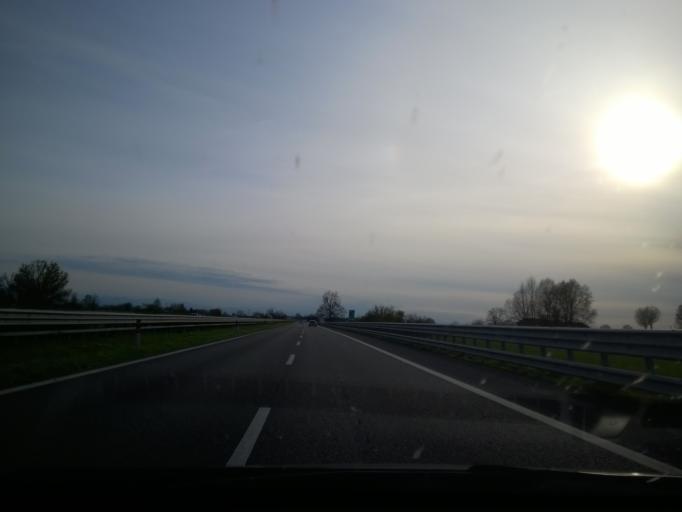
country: IT
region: Emilia-Romagna
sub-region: Provincia di Piacenza
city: Castelvetro Piacentino
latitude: 45.0761
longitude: 9.9703
